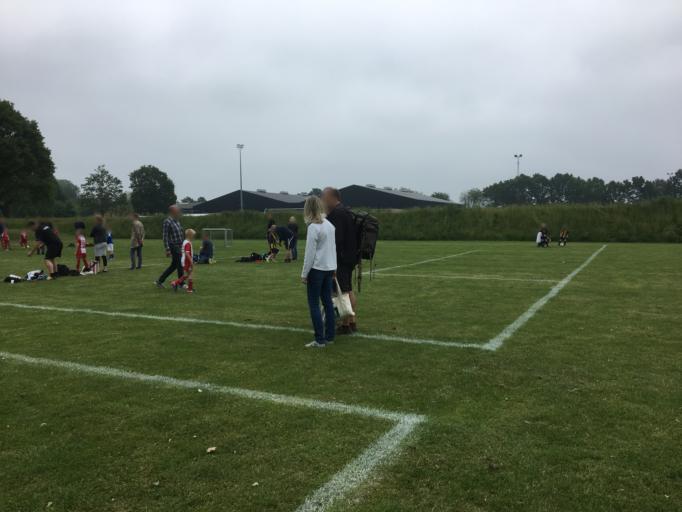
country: DK
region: South Denmark
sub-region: Odense Kommune
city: Stige
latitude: 55.4222
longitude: 10.3927
